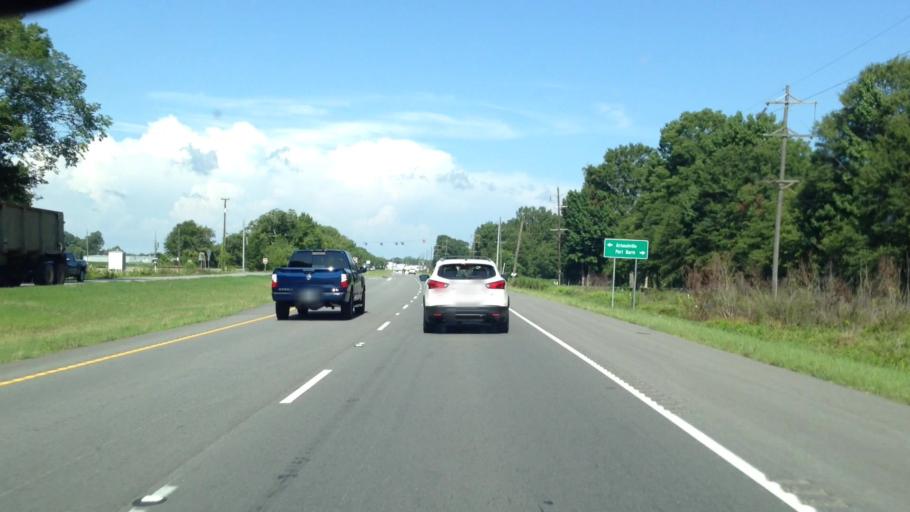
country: US
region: Louisiana
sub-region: Saint Landry Parish
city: Port Barre
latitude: 30.5474
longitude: -91.9460
